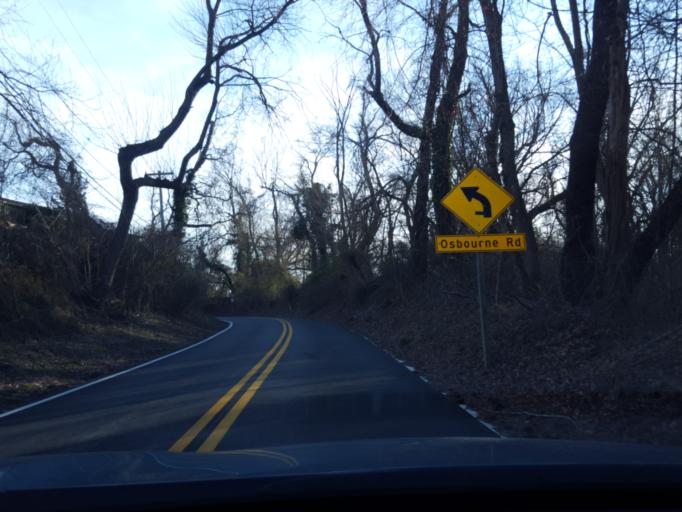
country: US
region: Maryland
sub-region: Anne Arundel County
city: Deale
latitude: 38.7470
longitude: -76.5594
